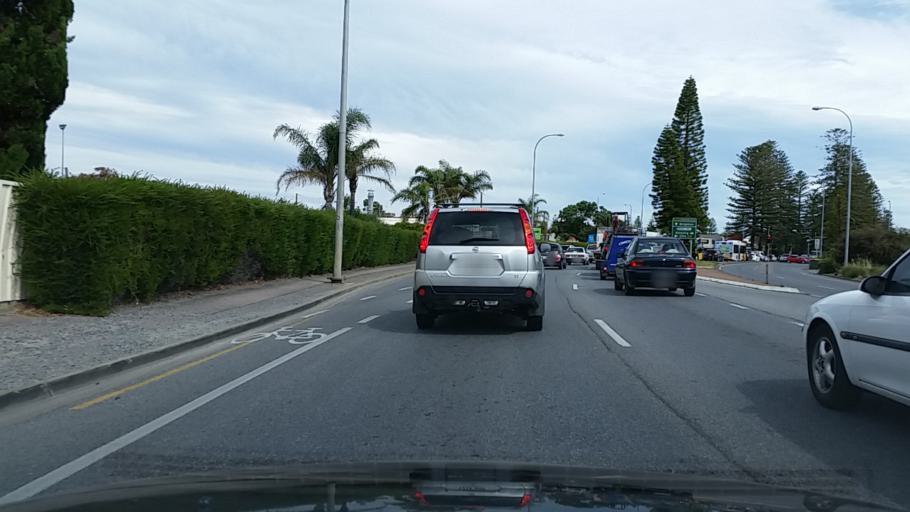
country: AU
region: South Australia
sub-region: Adelaide
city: Glenelg
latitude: -34.9749
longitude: 138.5195
